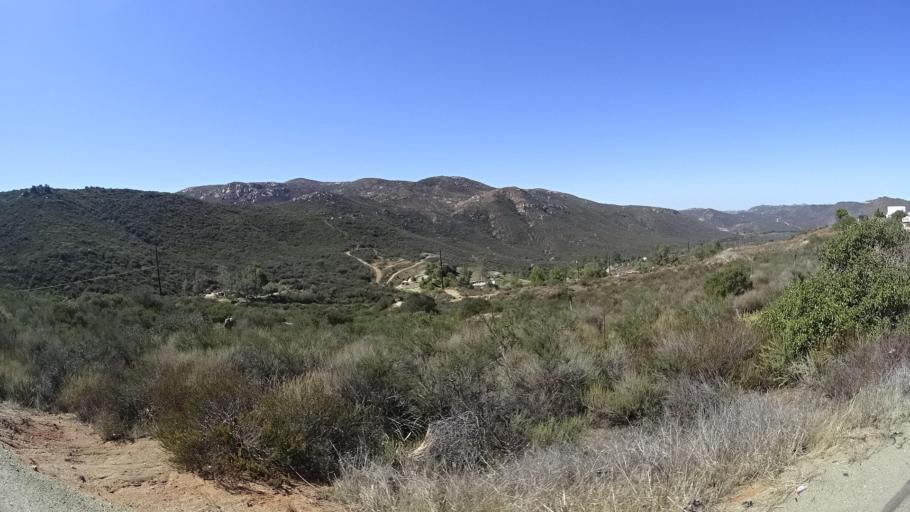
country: US
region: California
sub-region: San Diego County
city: Alpine
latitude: 32.7838
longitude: -116.7207
